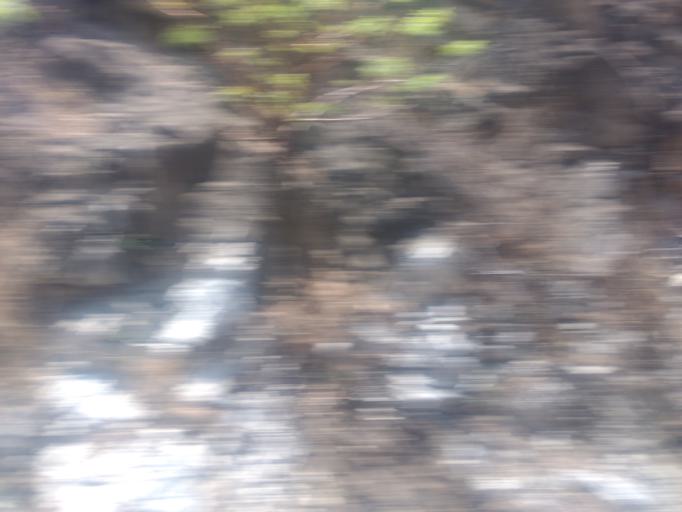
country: MX
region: Jalisco
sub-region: Tuxpan
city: La Higuera
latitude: 19.4979
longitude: -103.4424
